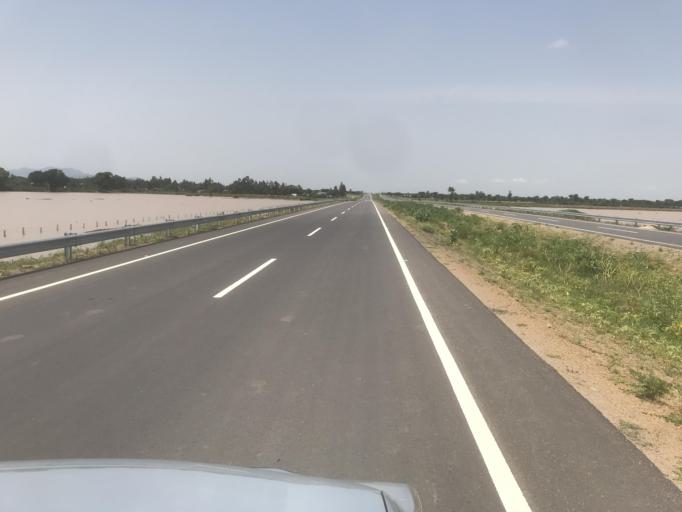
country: ET
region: Oromiya
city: Mojo
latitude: 8.3840
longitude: 39.0057
